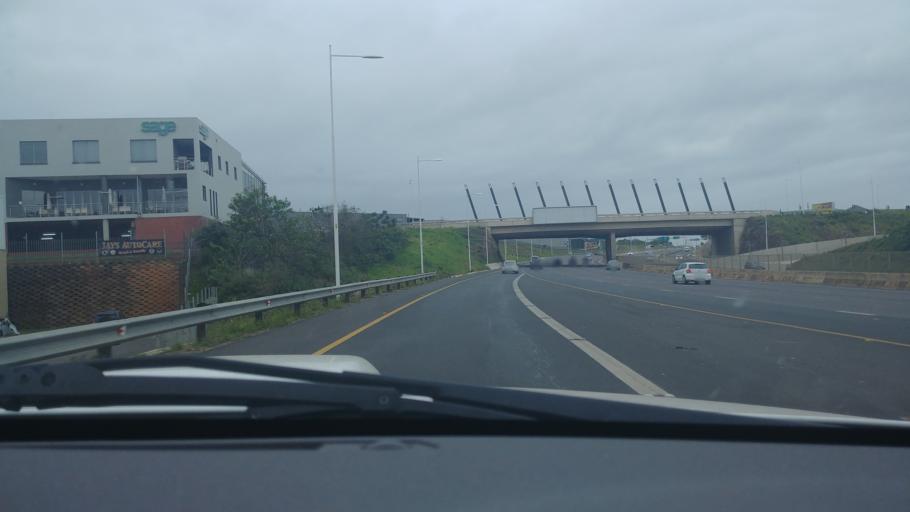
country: ZA
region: KwaZulu-Natal
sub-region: eThekwini Metropolitan Municipality
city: Durban
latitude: -29.7106
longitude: 31.0508
